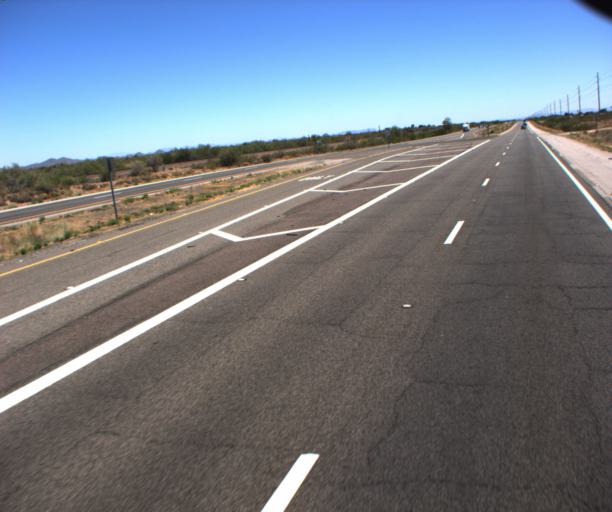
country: US
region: Arizona
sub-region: Maricopa County
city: Wickenburg
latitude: 33.7974
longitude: -112.5540
